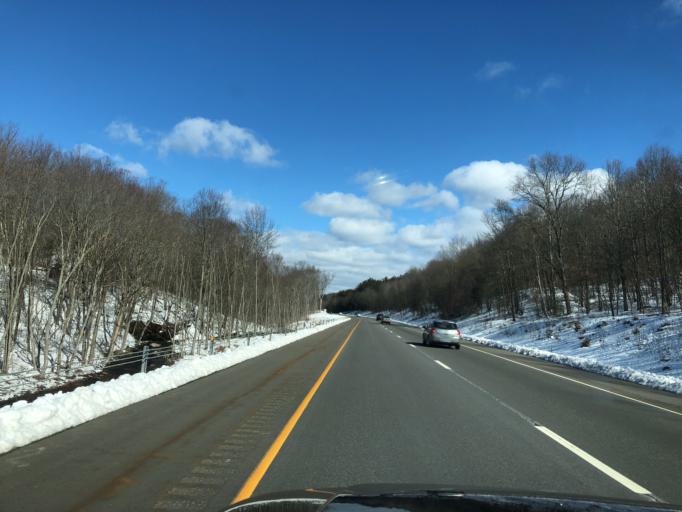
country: US
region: Connecticut
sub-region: Hartford County
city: Terramuggus
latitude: 41.6143
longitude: -72.4344
